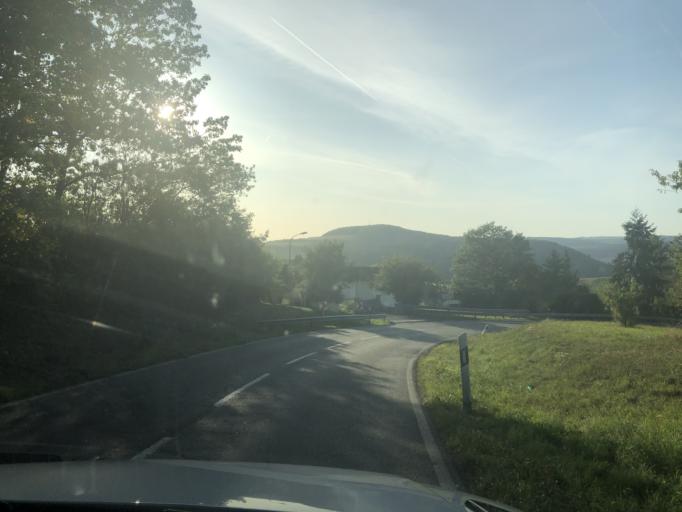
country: DE
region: Rheinland-Pfalz
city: Mertesdorf
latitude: 49.7712
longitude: 6.7397
